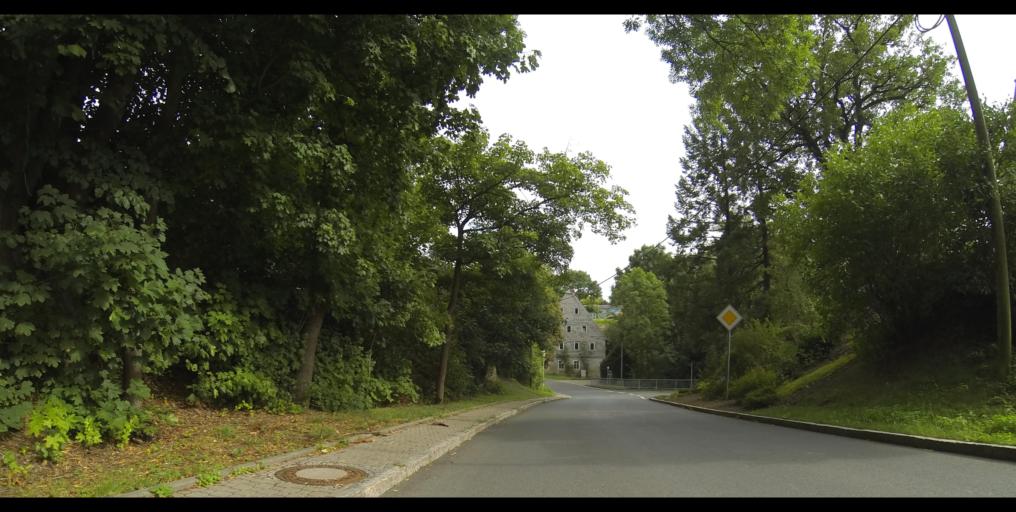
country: DE
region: Saxony
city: Grossschirma
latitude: 50.9874
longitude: 13.2399
